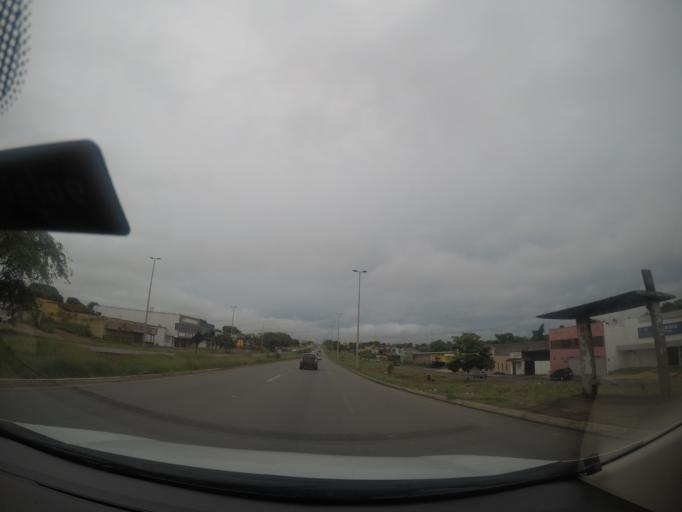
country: BR
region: Goias
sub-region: Aparecida De Goiania
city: Aparecida de Goiania
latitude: -16.7598
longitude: -49.3437
